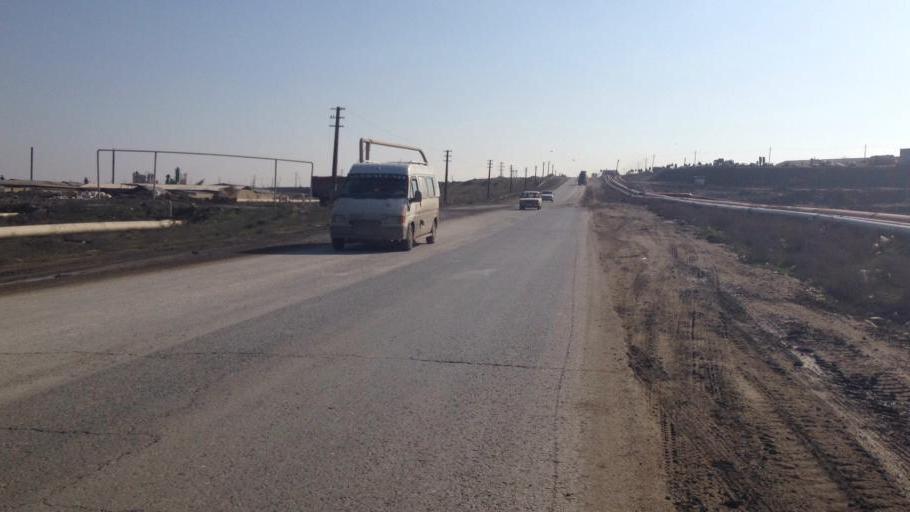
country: AZ
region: Abseron
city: Digah
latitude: 40.4667
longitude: 49.8869
